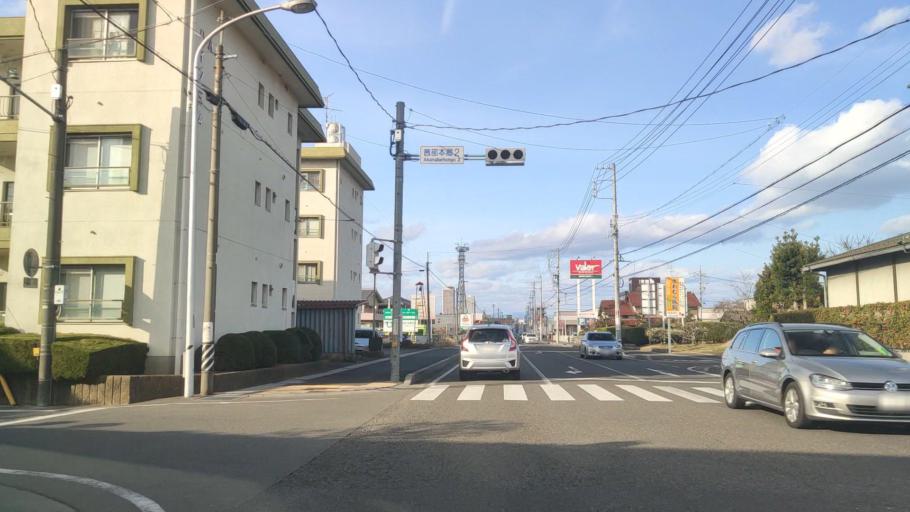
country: JP
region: Gifu
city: Kasamatsucho
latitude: 35.3899
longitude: 136.7547
